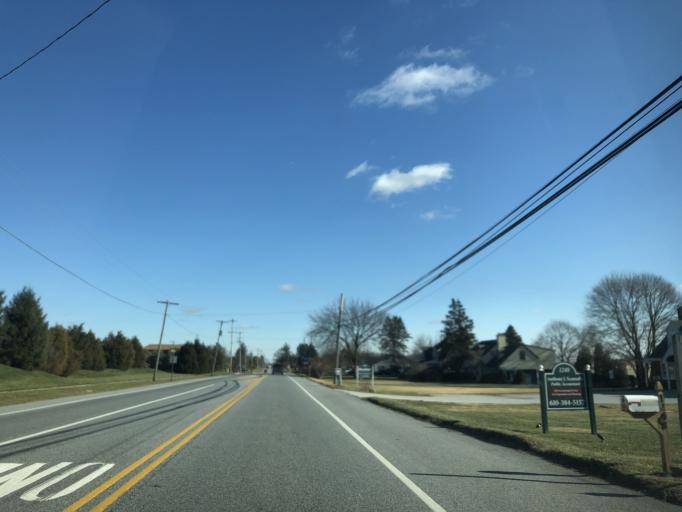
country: US
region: Pennsylvania
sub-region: Chester County
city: Parkesburg
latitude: 39.9828
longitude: -75.8778
